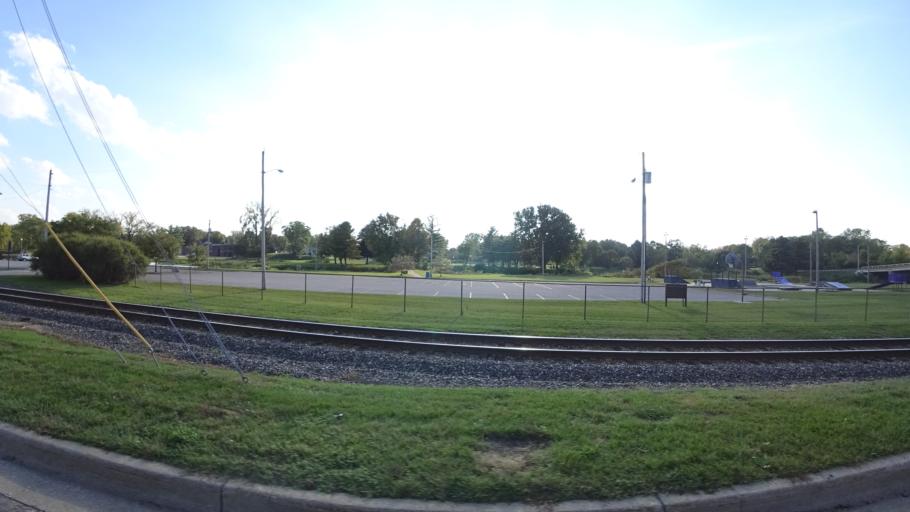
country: US
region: Michigan
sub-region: Saint Joseph County
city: Three Rivers
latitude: 41.9454
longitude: -85.6355
